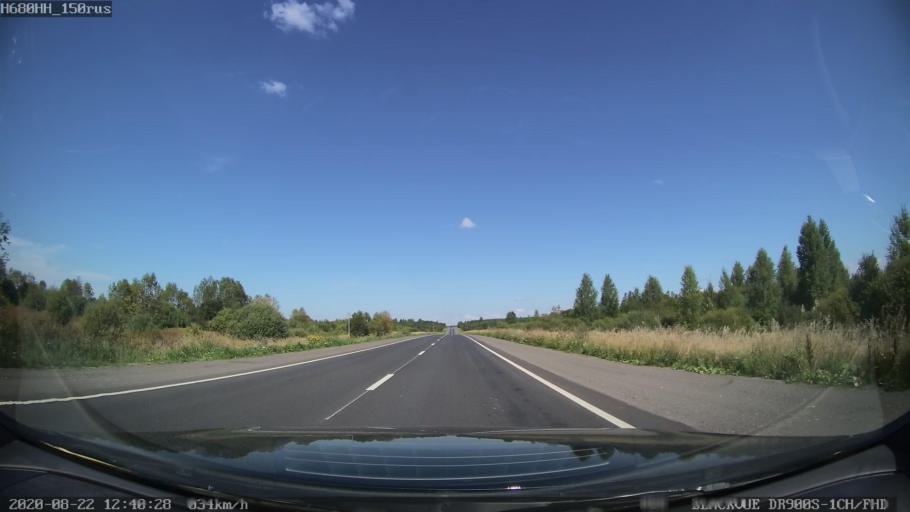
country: RU
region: Tverskaya
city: Rameshki
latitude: 57.3351
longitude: 36.0946
